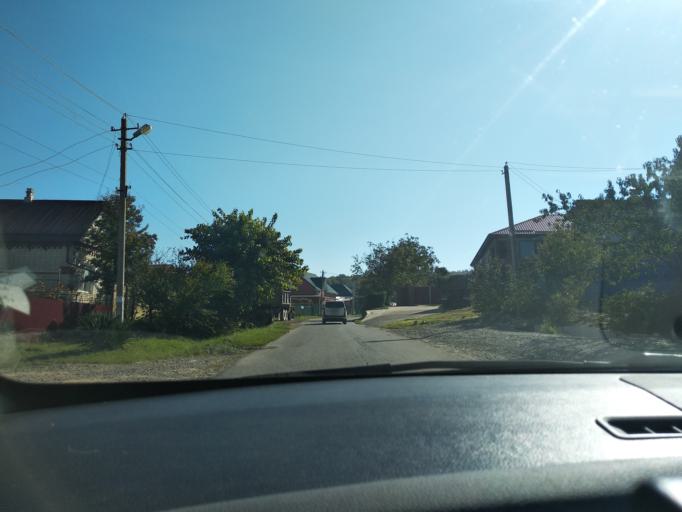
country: RU
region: Krasnodarskiy
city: Goryachiy Klyuch
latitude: 44.6303
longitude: 39.1553
